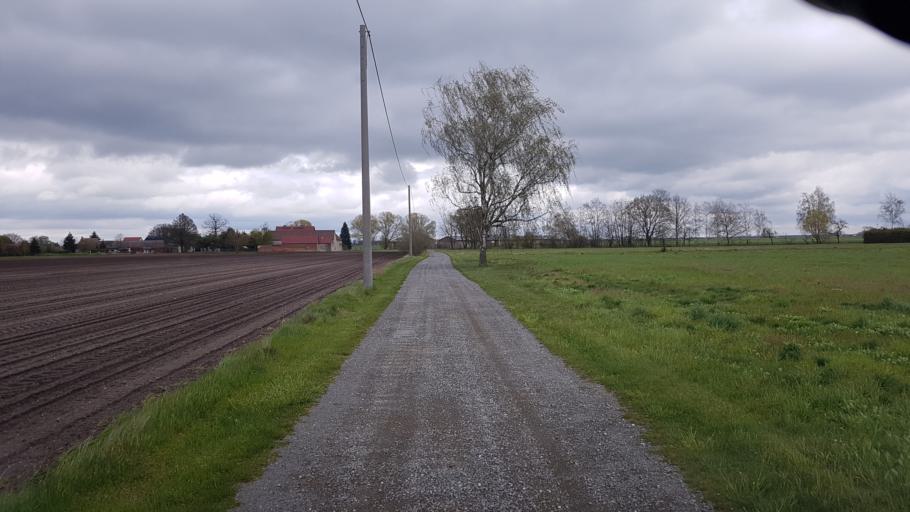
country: DE
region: Brandenburg
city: Schonborn
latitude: 51.6653
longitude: 13.5038
